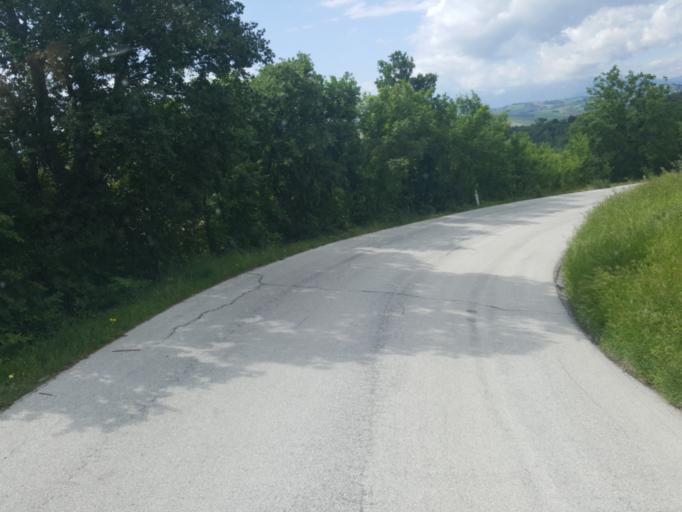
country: IT
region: The Marches
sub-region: Provincia di Macerata
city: Pollenza
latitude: 43.2546
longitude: 13.3687
